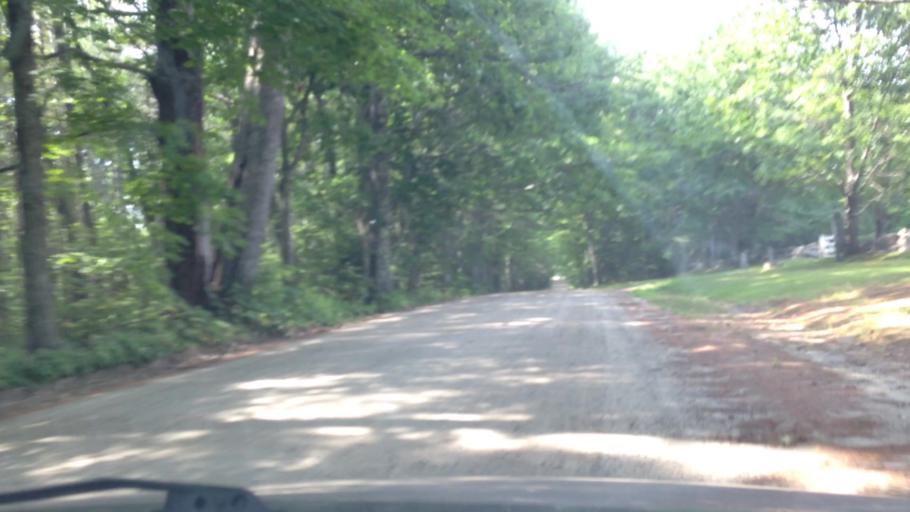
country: US
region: New Hampshire
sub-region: Cheshire County
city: Marlborough
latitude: 42.8851
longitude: -72.1897
